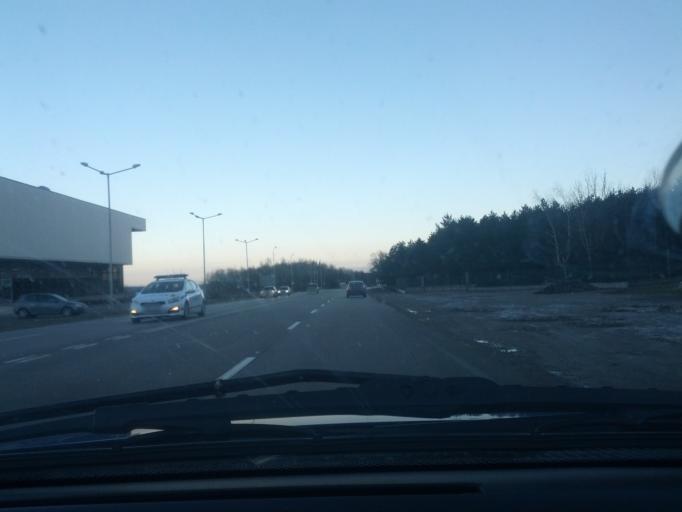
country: BG
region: Vratsa
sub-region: Obshtina Vratsa
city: Vratsa
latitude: 43.1850
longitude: 23.5858
